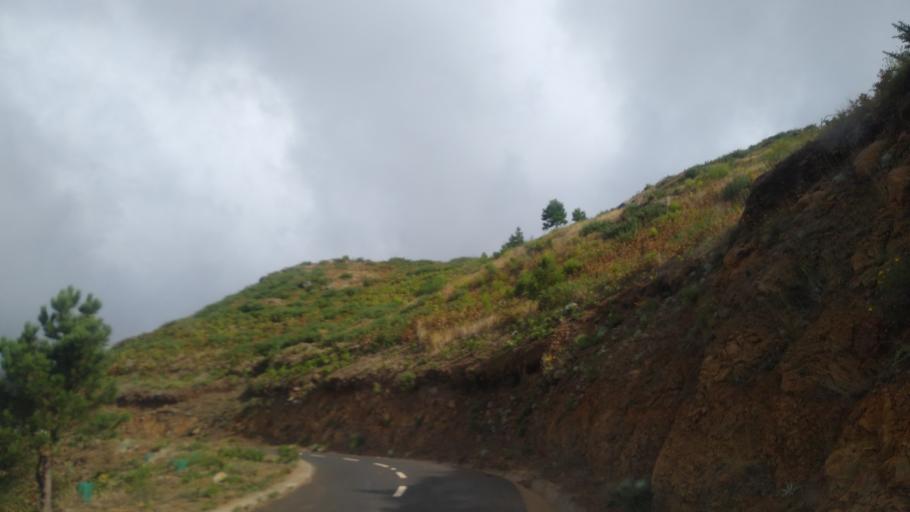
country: PT
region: Madeira
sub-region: Camara de Lobos
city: Curral das Freiras
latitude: 32.7014
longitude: -16.9397
